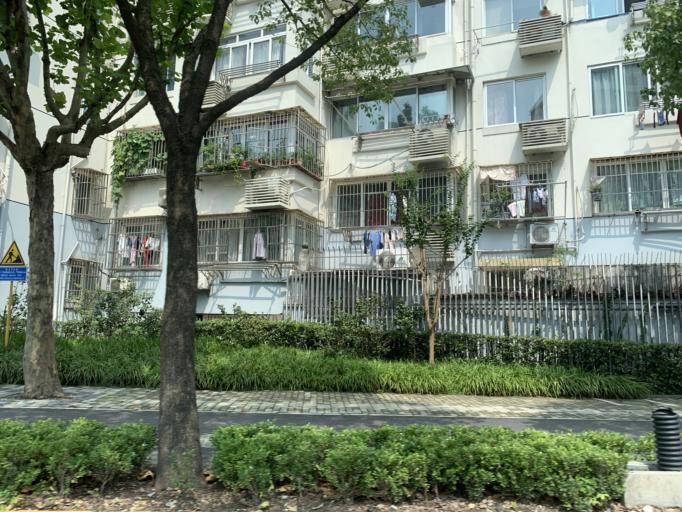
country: CN
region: Shanghai Shi
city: Luwan
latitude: 31.1826
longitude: 121.4944
